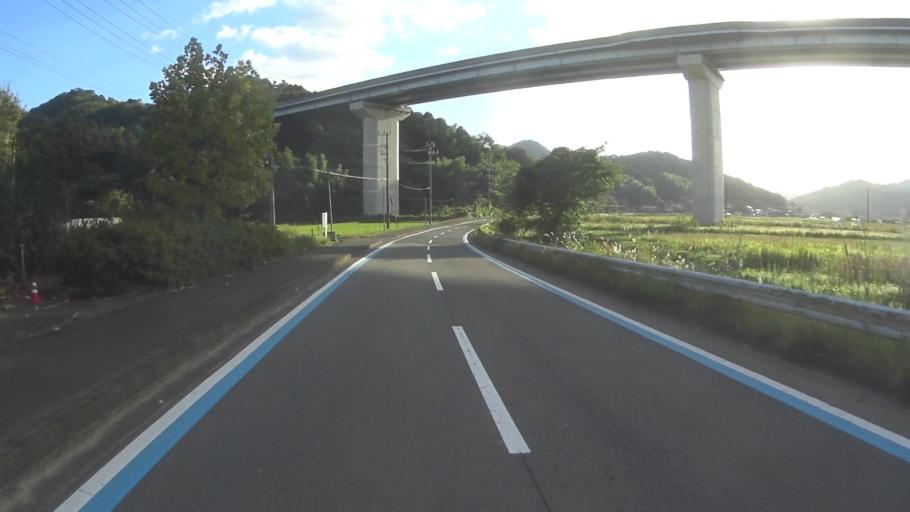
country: JP
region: Kyoto
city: Miyazu
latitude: 35.4214
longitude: 135.2138
